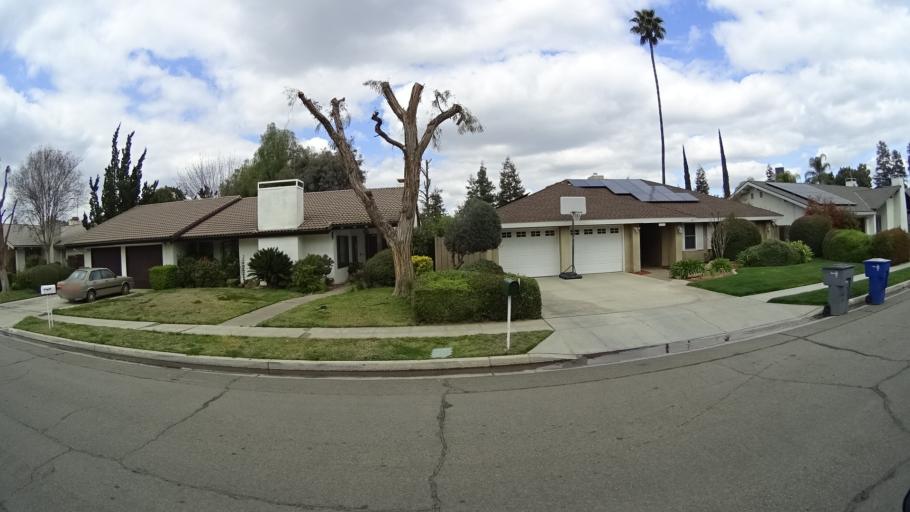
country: US
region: California
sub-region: Fresno County
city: Fresno
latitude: 36.8349
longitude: -119.8059
